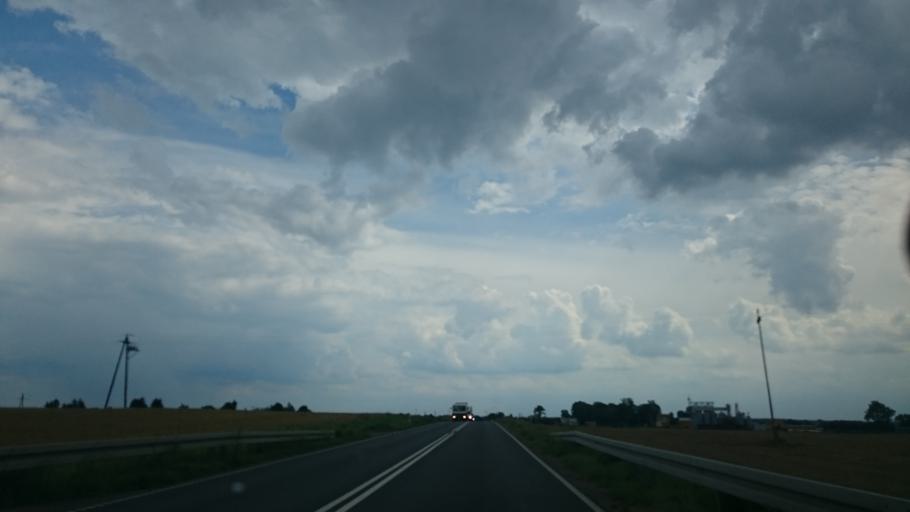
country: PL
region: Kujawsko-Pomorskie
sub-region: Powiat tucholski
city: Kesowo
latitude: 53.6583
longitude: 17.6857
